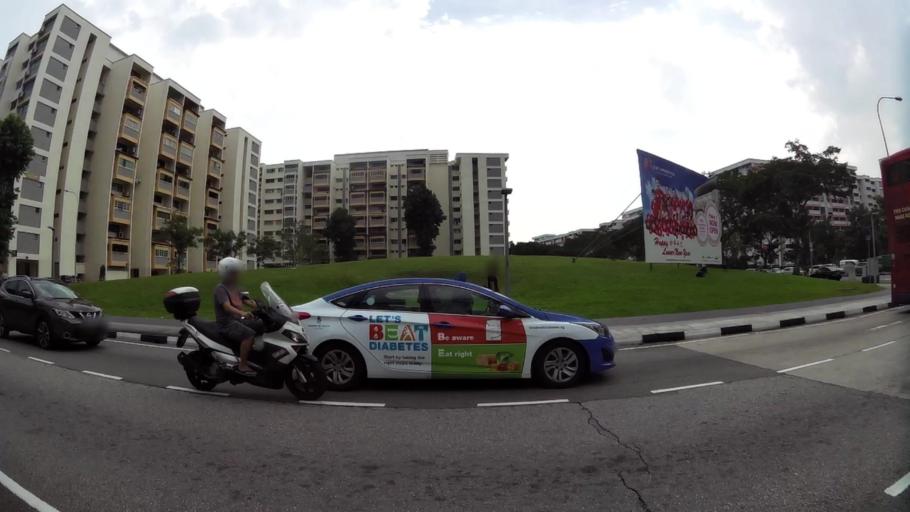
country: SG
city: Singapore
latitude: 1.3517
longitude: 103.9418
